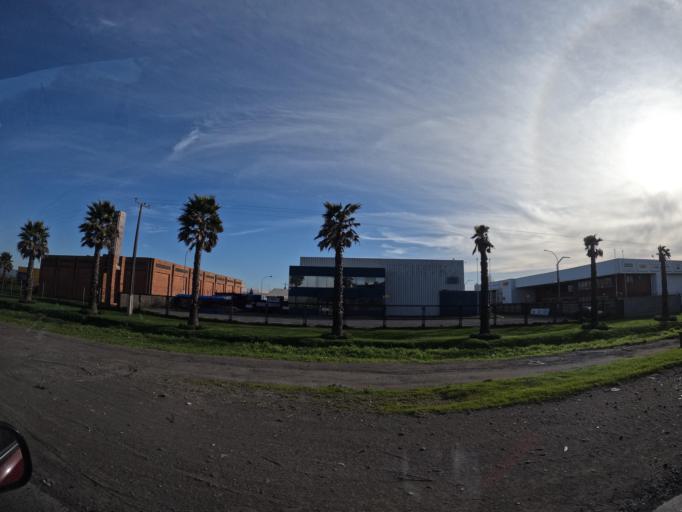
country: CL
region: Biobio
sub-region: Provincia de Concepcion
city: Concepcion
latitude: -36.7828
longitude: -73.0760
